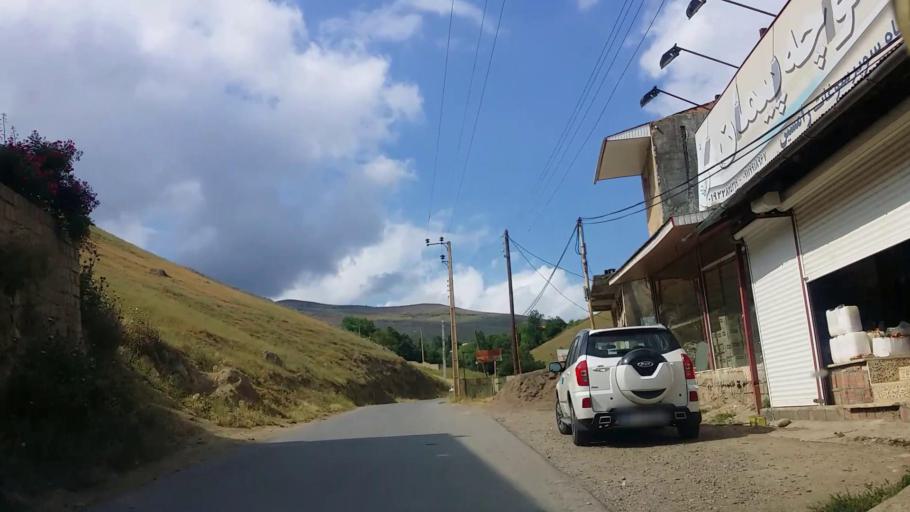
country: IR
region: Mazandaran
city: Chalus
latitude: 36.5157
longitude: 51.2592
